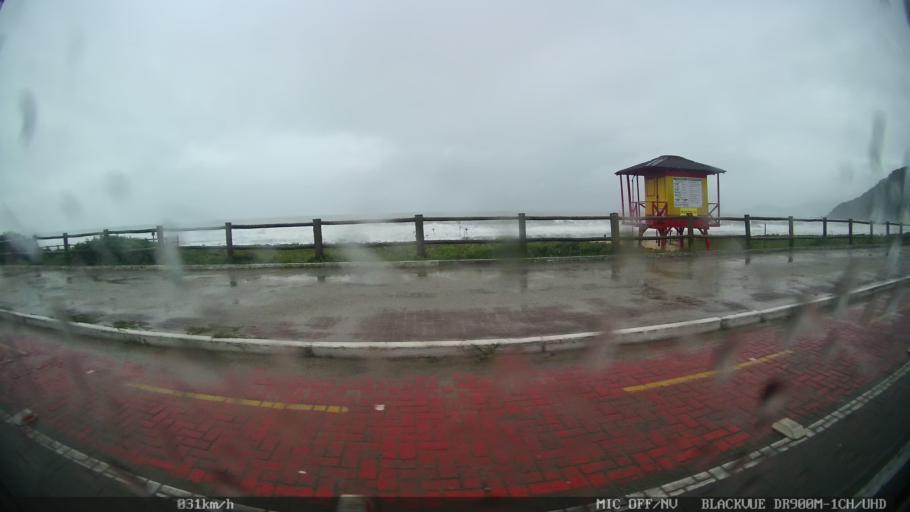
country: BR
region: Santa Catarina
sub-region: Balneario Camboriu
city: Balneario Camboriu
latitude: -26.9540
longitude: -48.6298
